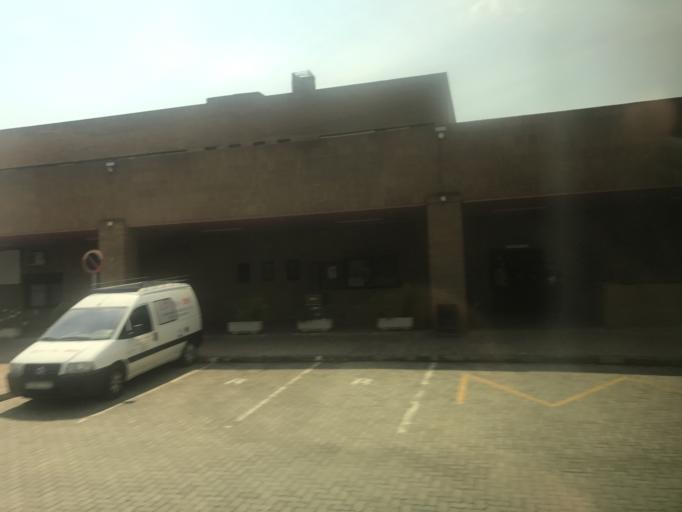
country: ES
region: Castille and Leon
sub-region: Provincia de Palencia
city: Palencia
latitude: 42.0165
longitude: -4.5366
